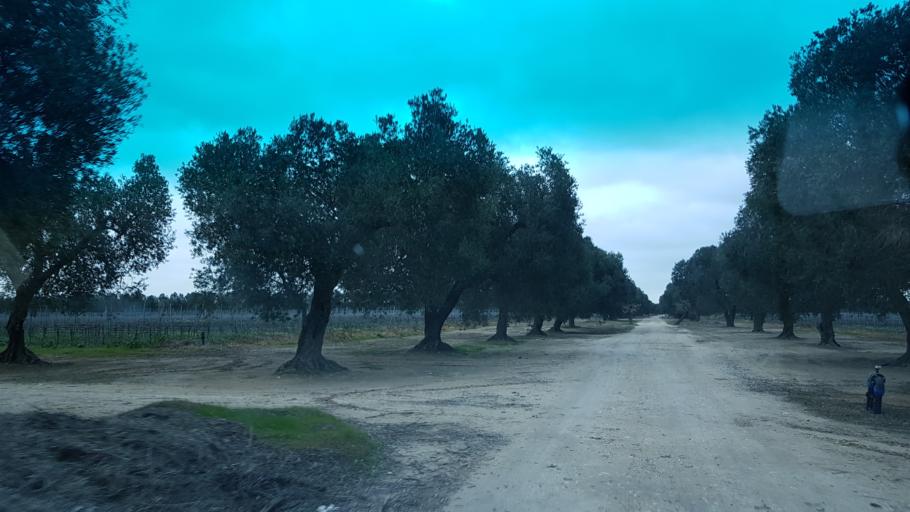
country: IT
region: Apulia
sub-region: Provincia di Brindisi
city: La Rosa
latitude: 40.5914
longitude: 17.9806
